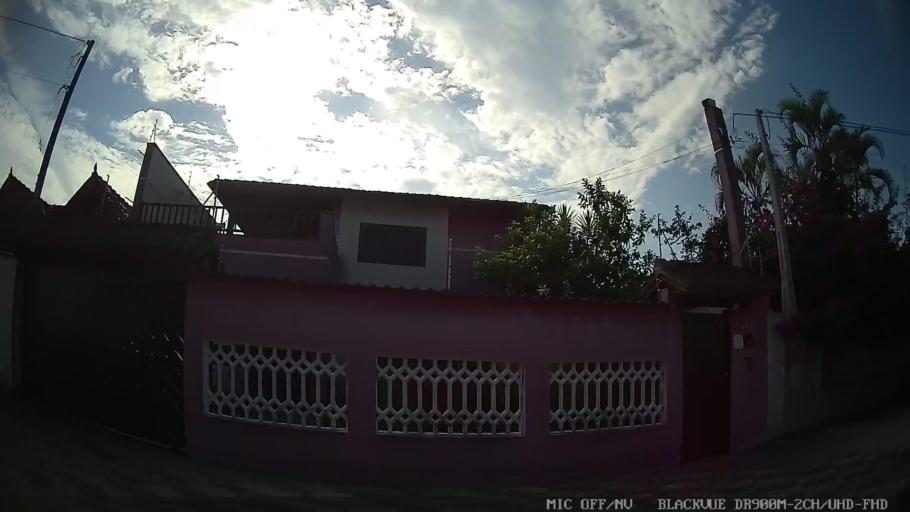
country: BR
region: Sao Paulo
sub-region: Caraguatatuba
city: Caraguatatuba
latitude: -23.6588
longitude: -45.4336
